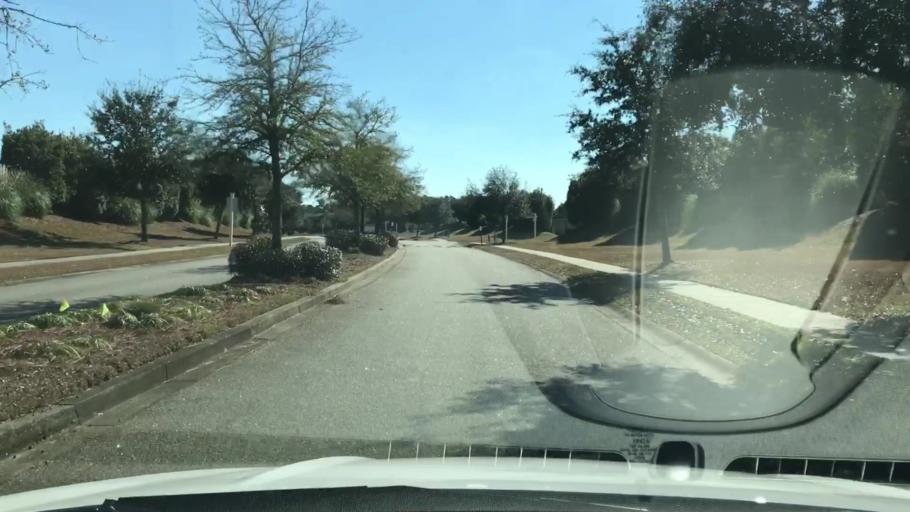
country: US
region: South Carolina
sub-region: Horry County
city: Socastee
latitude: 33.6455
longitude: -79.0373
